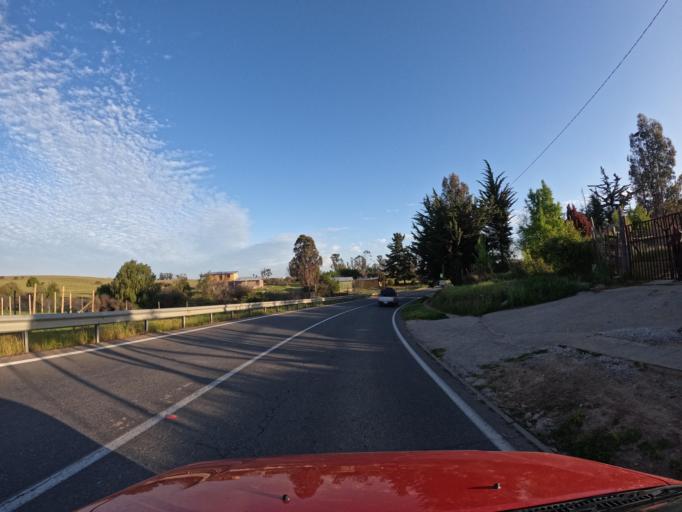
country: CL
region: O'Higgins
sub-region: Provincia de Colchagua
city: Santa Cruz
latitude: -34.2415
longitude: -71.7272
